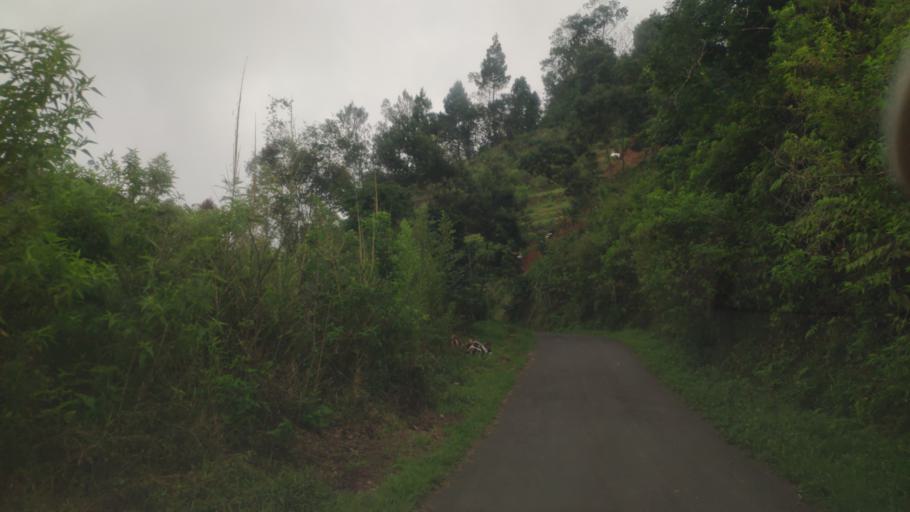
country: ID
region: Central Java
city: Wonosobo
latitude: -7.2289
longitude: 109.7991
